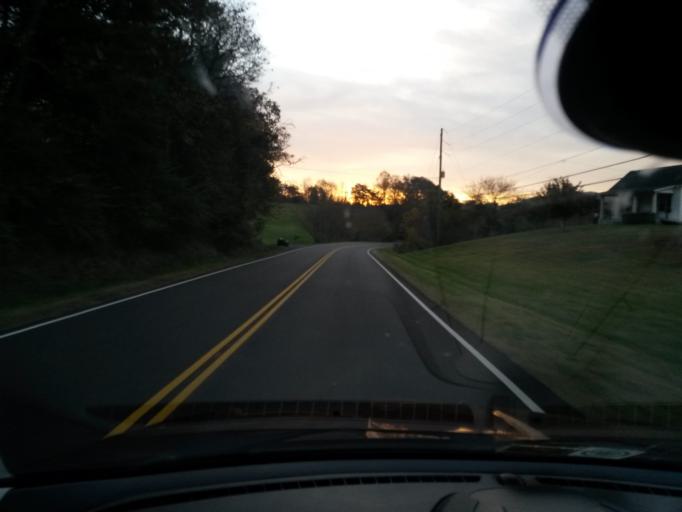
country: US
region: Virginia
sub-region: City of Roanoke
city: Cedar Bluff
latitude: 37.2223
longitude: -79.8955
